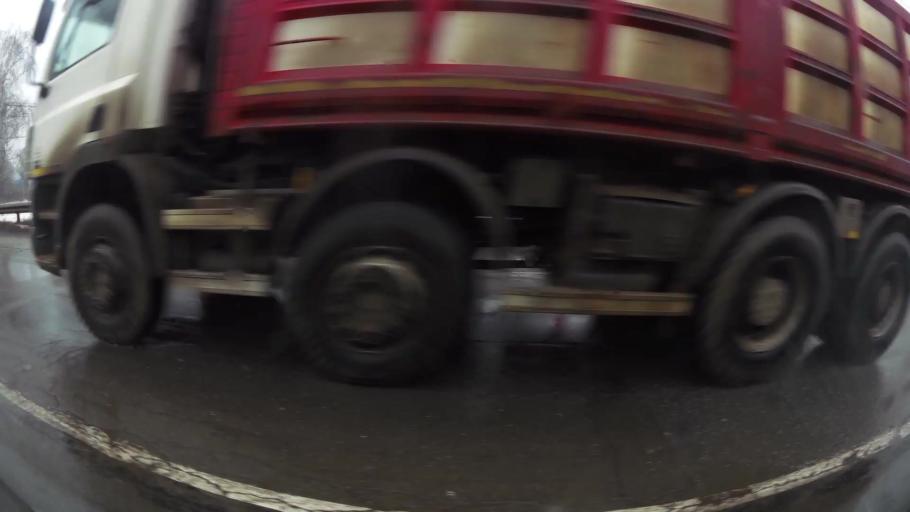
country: BG
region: Sofiya
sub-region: Obshtina Bozhurishte
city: Bozhurishte
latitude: 42.6912
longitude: 23.2302
